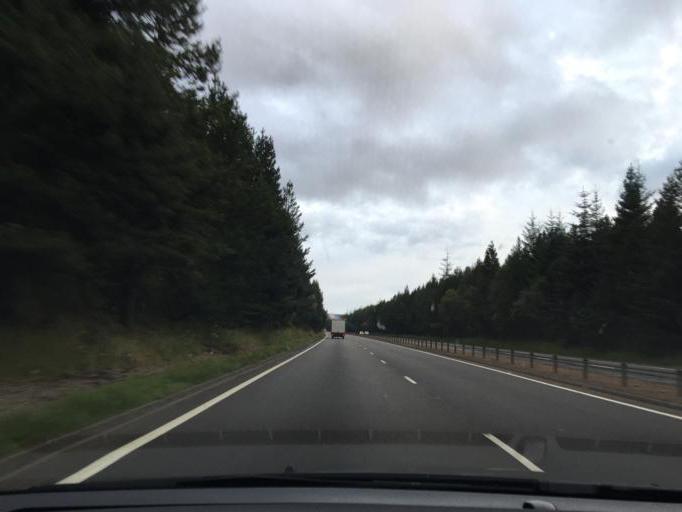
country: GB
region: Scotland
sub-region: Highland
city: Inverness
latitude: 57.4017
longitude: -4.1313
